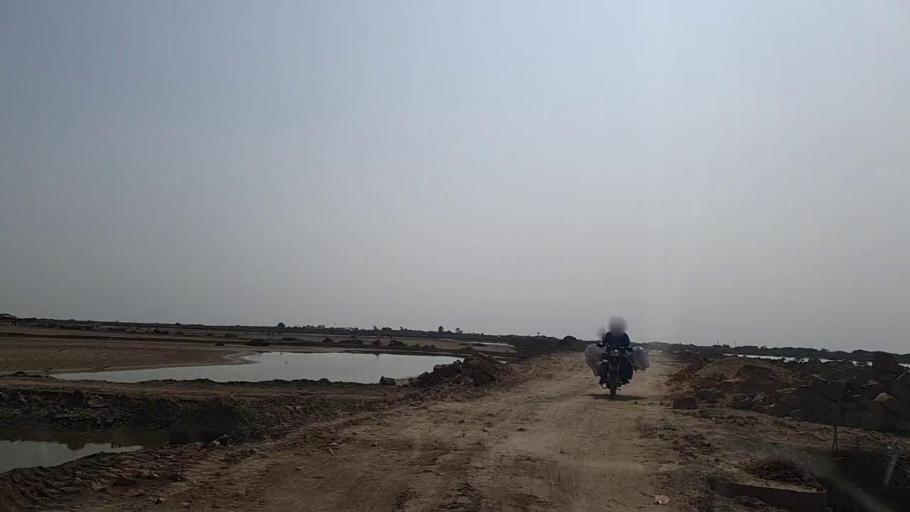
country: PK
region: Sindh
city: Chuhar Jamali
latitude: 24.1975
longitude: 67.8488
